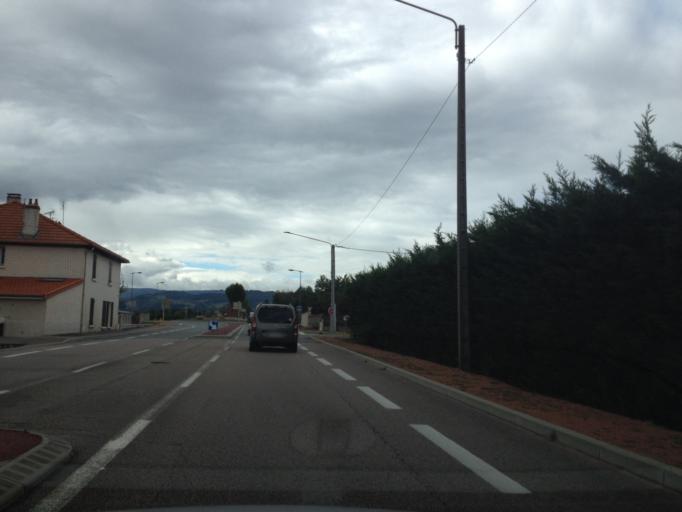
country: FR
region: Rhone-Alpes
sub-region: Departement de la Loire
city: Pouilly-les-Nonains
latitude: 46.0473
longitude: 3.9867
